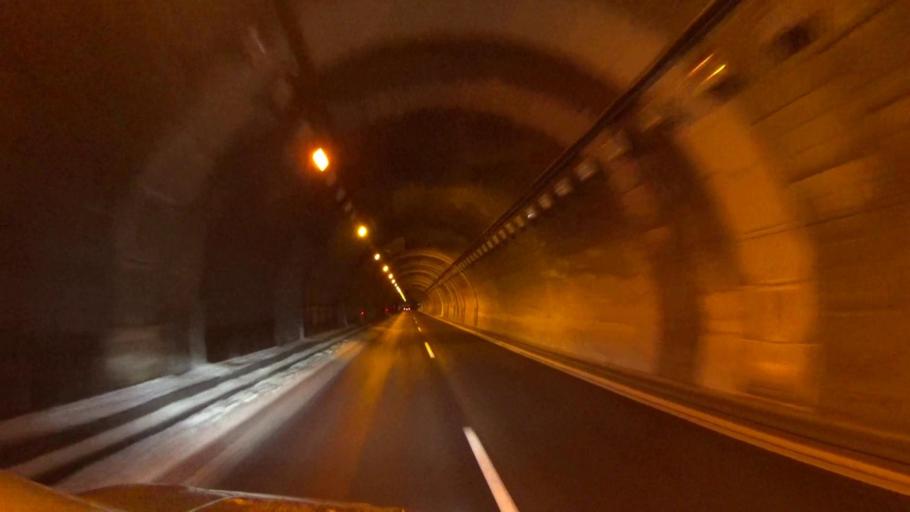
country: JP
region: Hokkaido
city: Otaru
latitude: 43.1756
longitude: 141.0277
